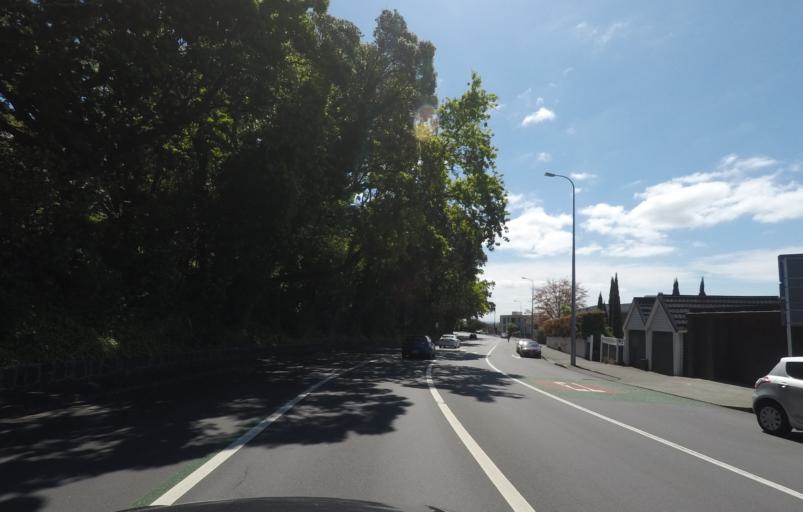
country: NZ
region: Auckland
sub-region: Auckland
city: Auckland
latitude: -36.8783
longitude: 174.7896
